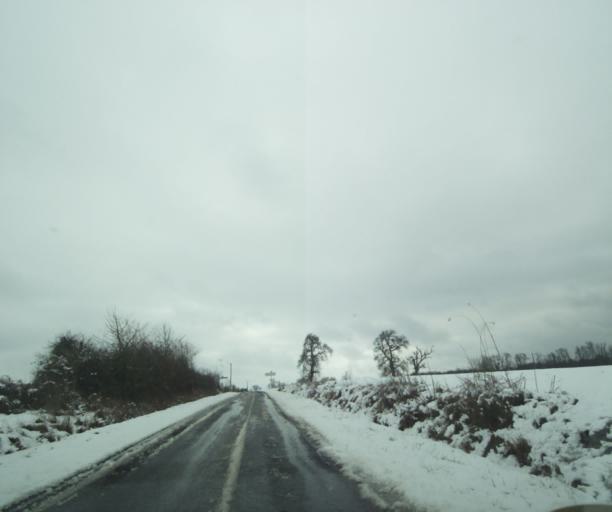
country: FR
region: Champagne-Ardenne
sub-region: Departement de la Haute-Marne
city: Montier-en-Der
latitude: 48.4151
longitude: 4.7349
